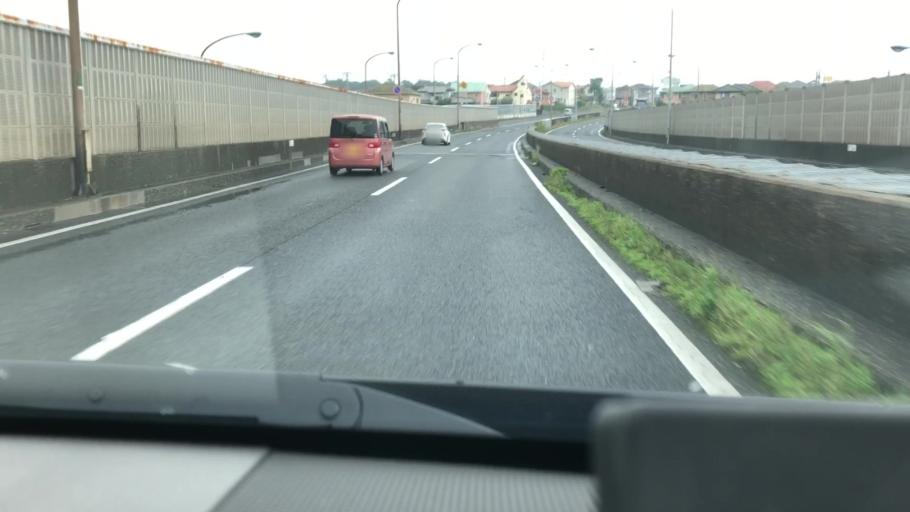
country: JP
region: Chiba
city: Kisarazu
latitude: 35.4362
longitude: 139.9705
